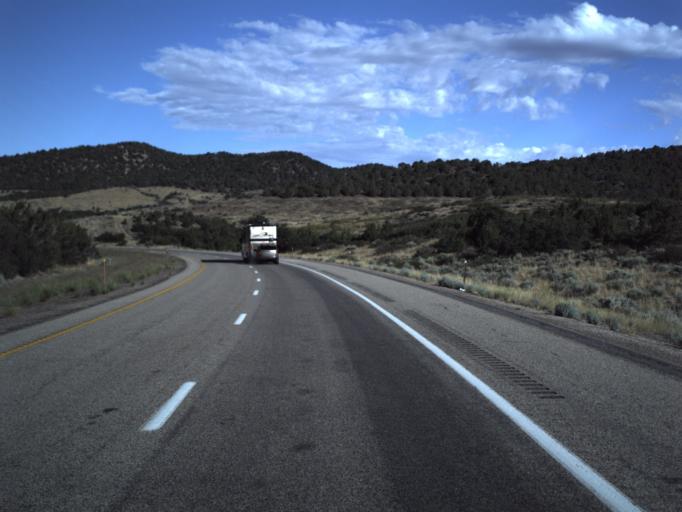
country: US
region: Utah
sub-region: Beaver County
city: Beaver
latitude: 38.6069
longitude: -112.5082
